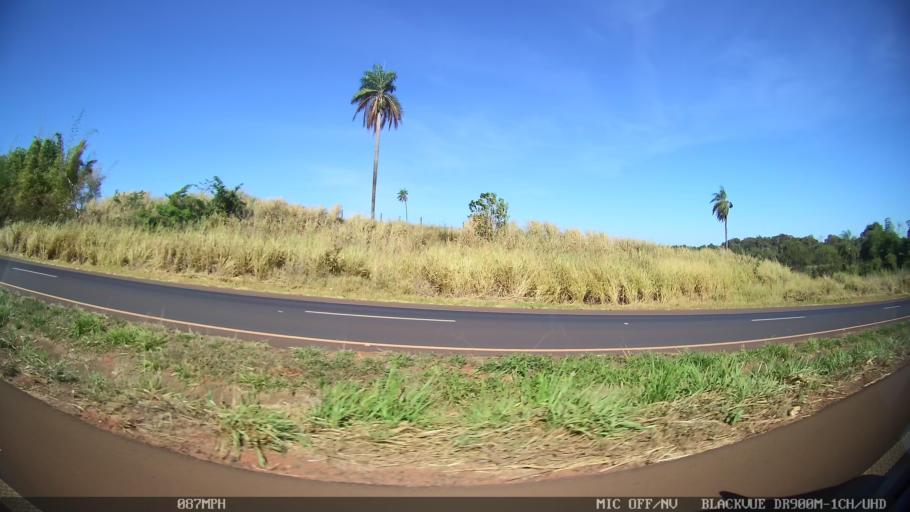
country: BR
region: Sao Paulo
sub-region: Barretos
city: Barretos
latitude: -20.5231
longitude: -48.5825
